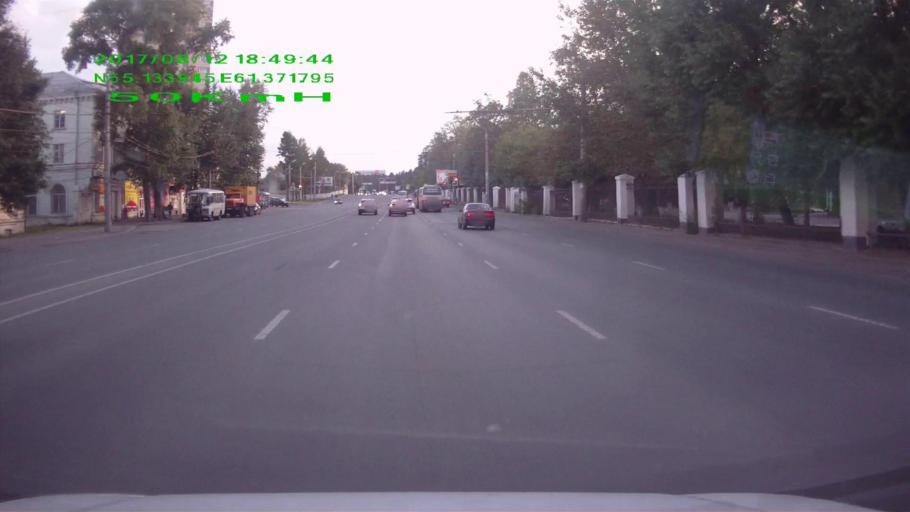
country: RU
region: Chelyabinsk
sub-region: Gorod Chelyabinsk
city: Chelyabinsk
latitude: 55.1302
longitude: 61.3669
